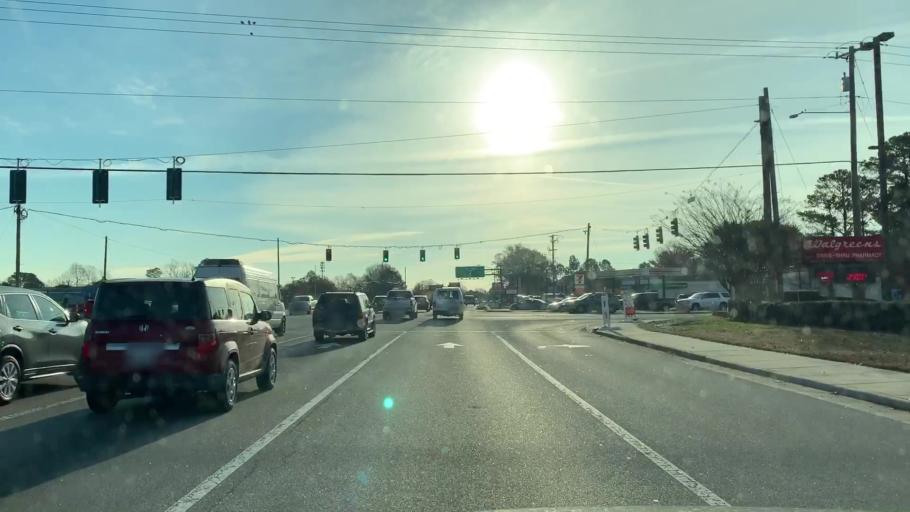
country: US
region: Virginia
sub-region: City of Chesapeake
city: Chesapeake
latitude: 36.7976
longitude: -76.1754
